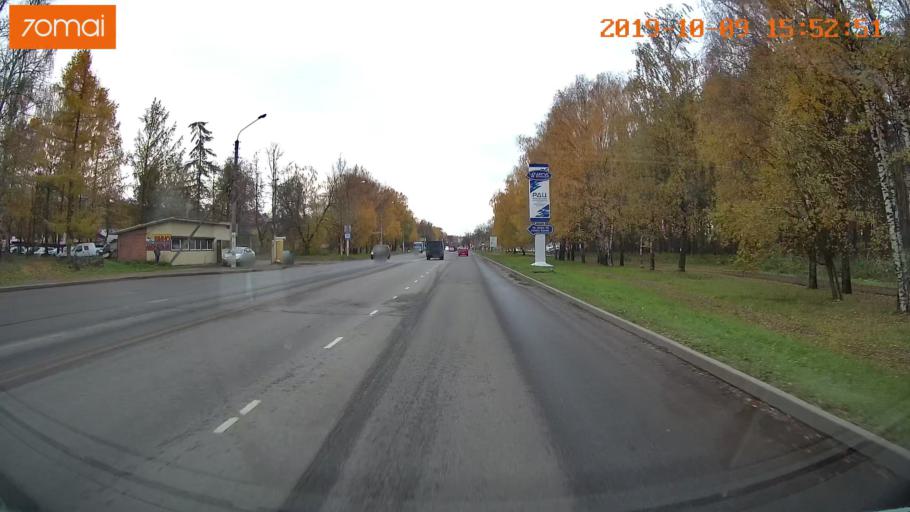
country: RU
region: Kostroma
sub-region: Kostromskoy Rayon
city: Kostroma
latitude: 57.7864
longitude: 40.9632
